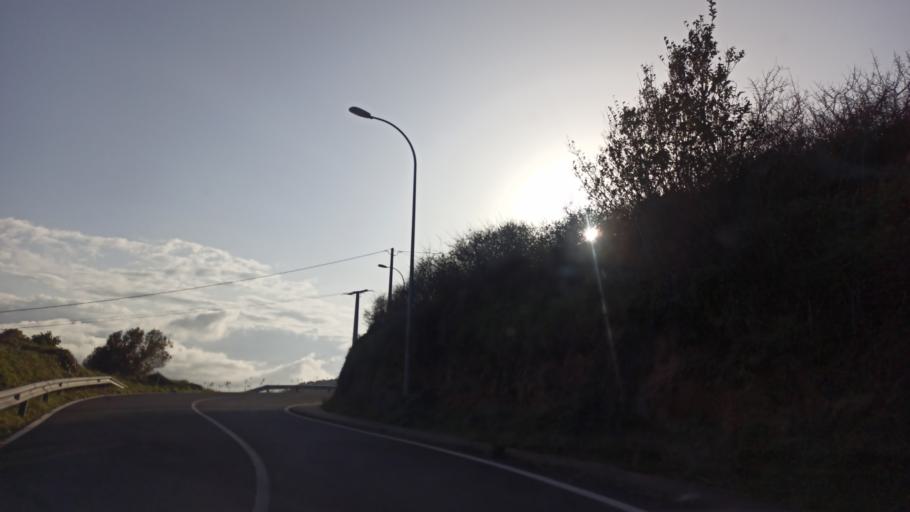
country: ES
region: Galicia
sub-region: Provincia de Lugo
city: Viveiro
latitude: 43.7732
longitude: -7.6717
